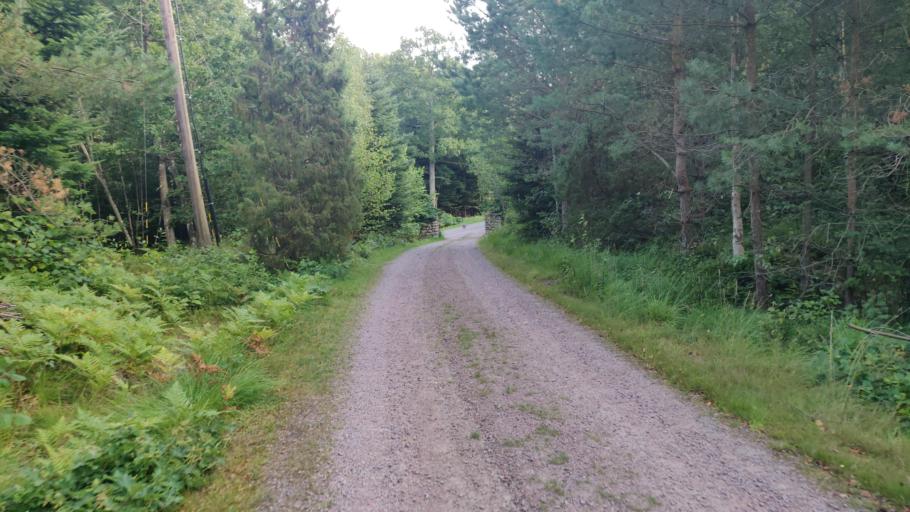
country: SE
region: Vaestra Goetaland
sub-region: Goteborg
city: Torslanda
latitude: 57.7853
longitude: 11.8316
